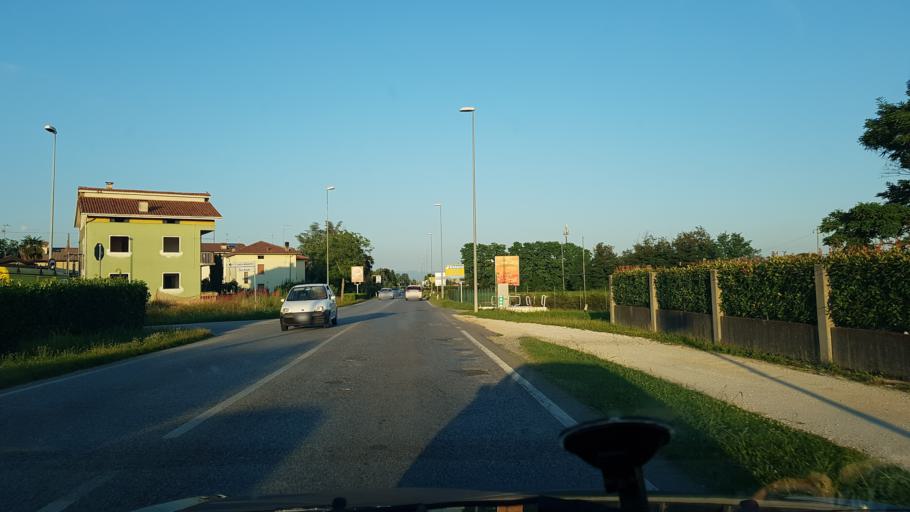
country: IT
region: Friuli Venezia Giulia
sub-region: Provincia di Udine
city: Martignacco
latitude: 46.0910
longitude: 13.1364
